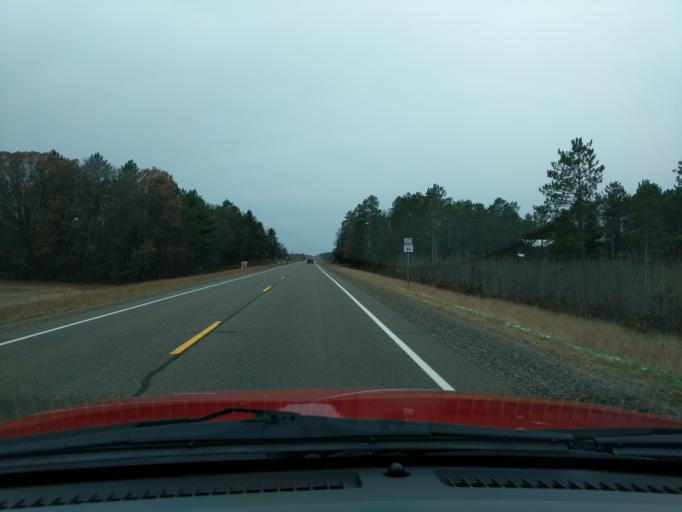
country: US
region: Wisconsin
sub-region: Washburn County
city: Shell Lake
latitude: 45.8155
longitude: -92.0887
